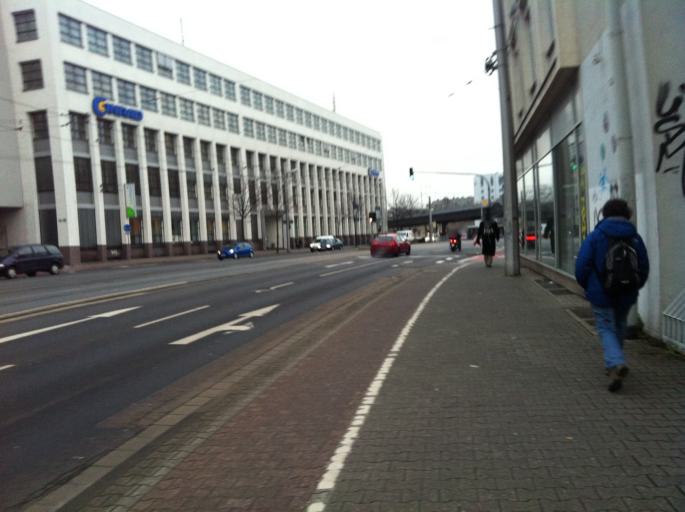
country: DE
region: Rheinland-Pfalz
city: Mainz
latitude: 49.9987
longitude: 8.2573
